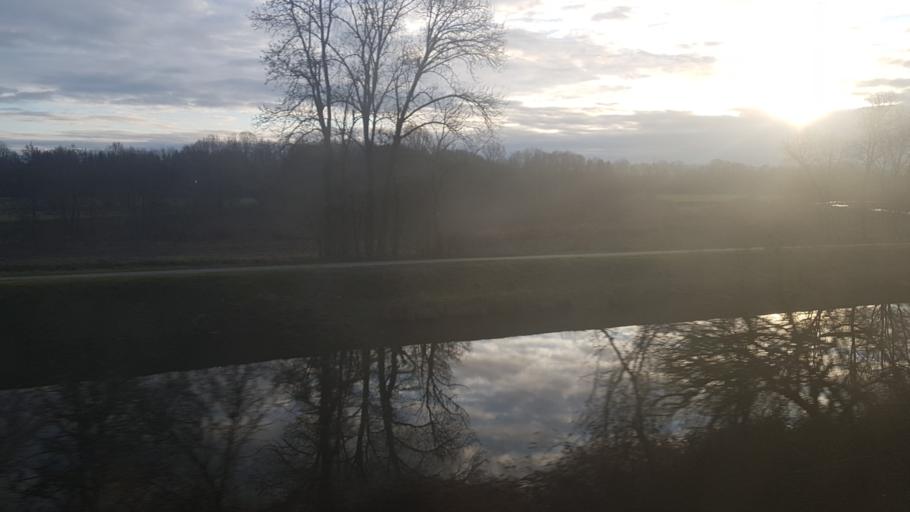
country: FR
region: Lorraine
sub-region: Departement des Vosges
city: Igney
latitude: 48.2892
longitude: 6.3974
